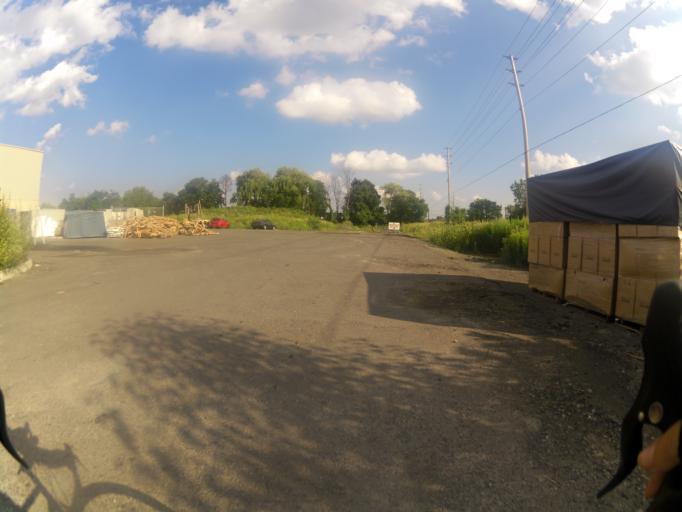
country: CA
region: Ontario
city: Ottawa
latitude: 45.3285
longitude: -75.7241
